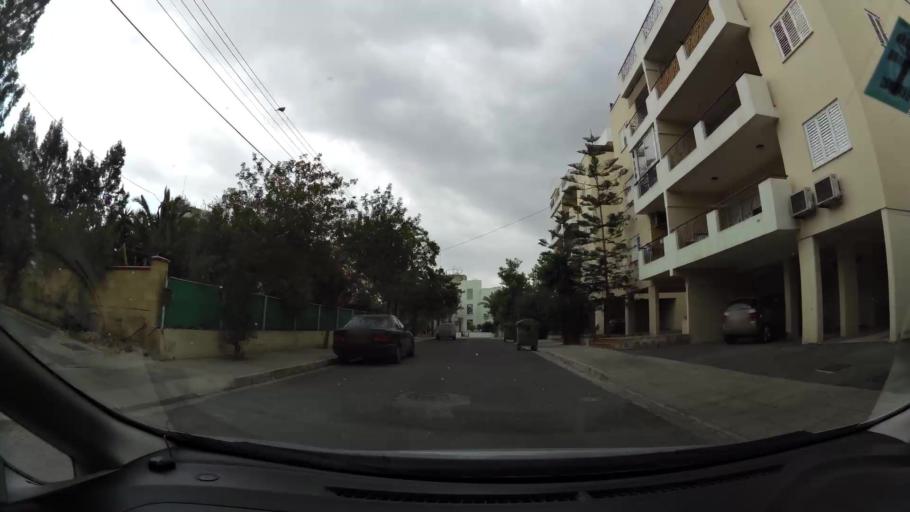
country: CY
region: Lefkosia
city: Nicosia
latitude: 35.1571
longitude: 33.3562
